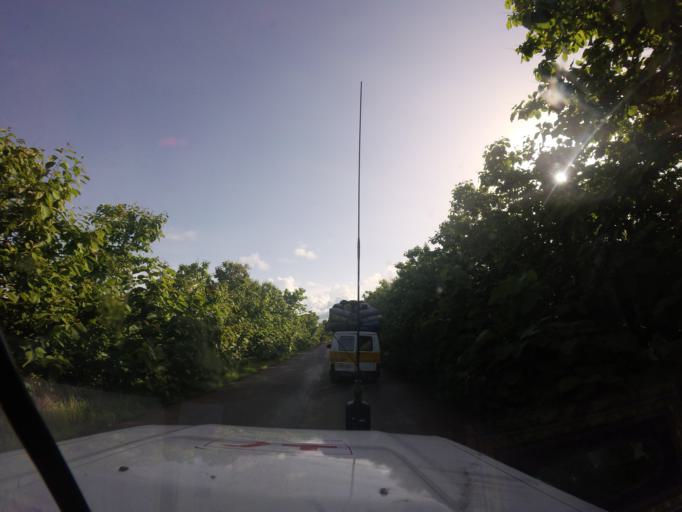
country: GN
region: Kindia
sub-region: Kindia
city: Kindia
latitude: 9.9913
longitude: -12.7426
